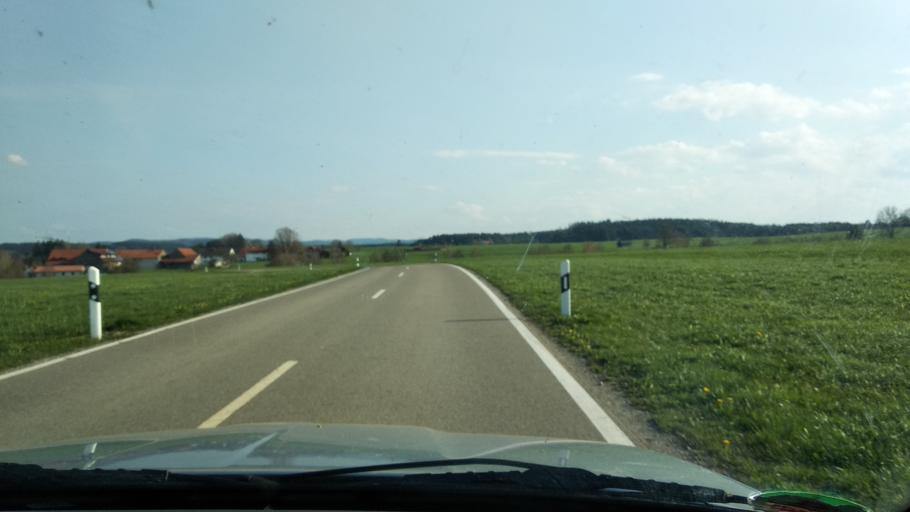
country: DE
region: Bavaria
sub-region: Swabia
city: Legau
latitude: 47.8389
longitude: 10.0900
